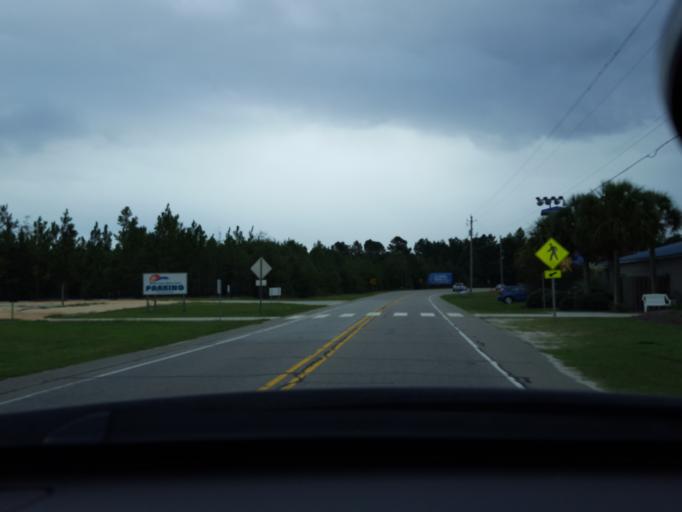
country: US
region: North Carolina
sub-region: Bladen County
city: Elizabethtown
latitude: 34.6484
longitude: -78.5208
